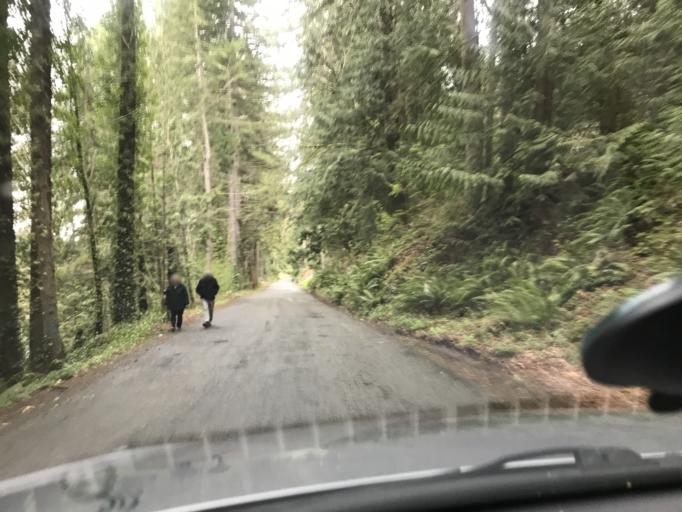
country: US
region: Washington
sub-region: King County
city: Ames Lake
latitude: 47.6417
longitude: -121.9532
